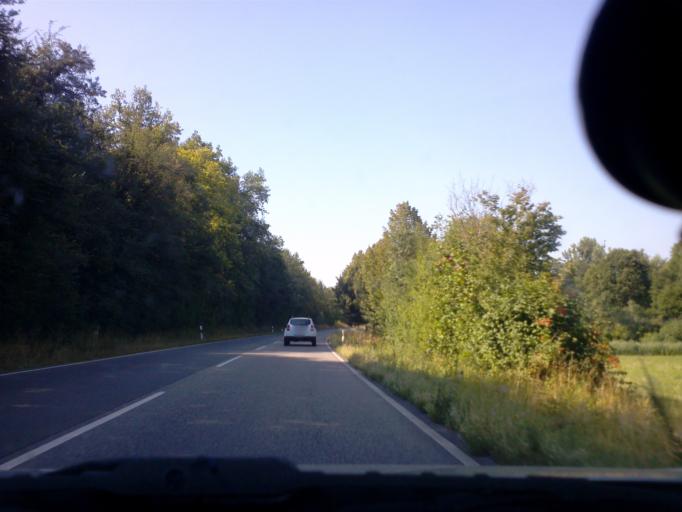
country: DE
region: Baden-Wuerttemberg
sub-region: Karlsruhe Region
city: Weingarten
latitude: 49.0711
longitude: 8.5420
